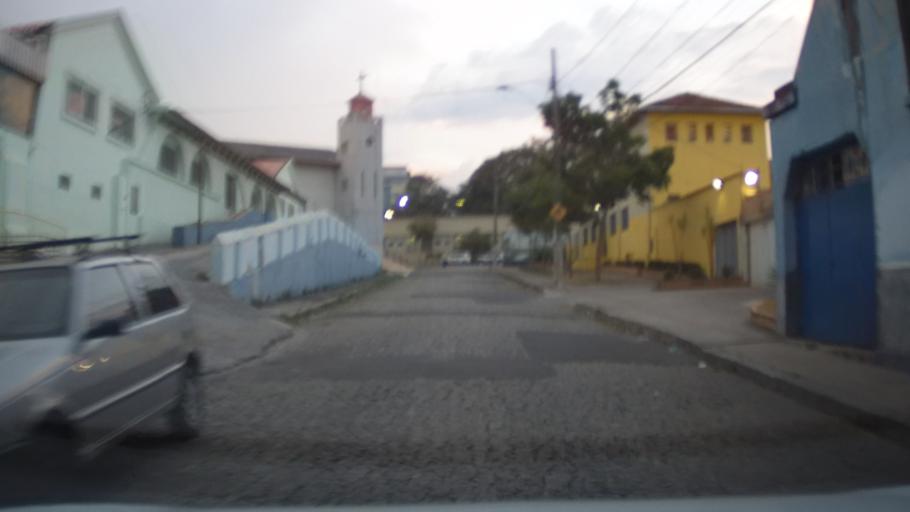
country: BR
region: Minas Gerais
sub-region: Belo Horizonte
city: Belo Horizonte
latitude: -19.8853
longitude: -43.9306
